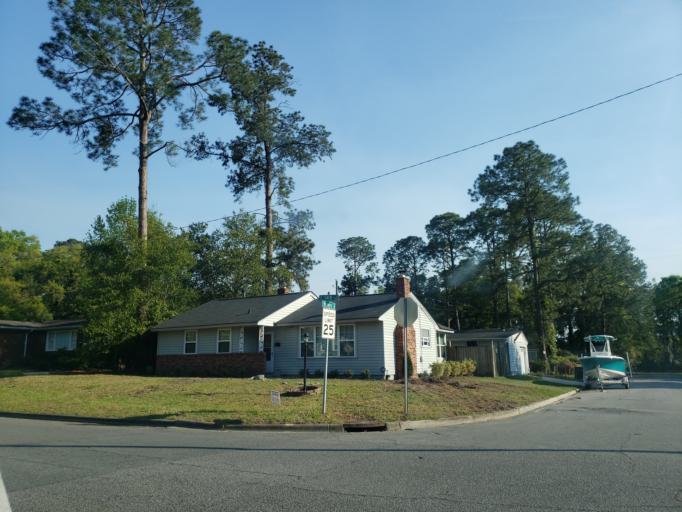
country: US
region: Georgia
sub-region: Chatham County
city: Thunderbolt
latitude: 32.0379
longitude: -81.0814
